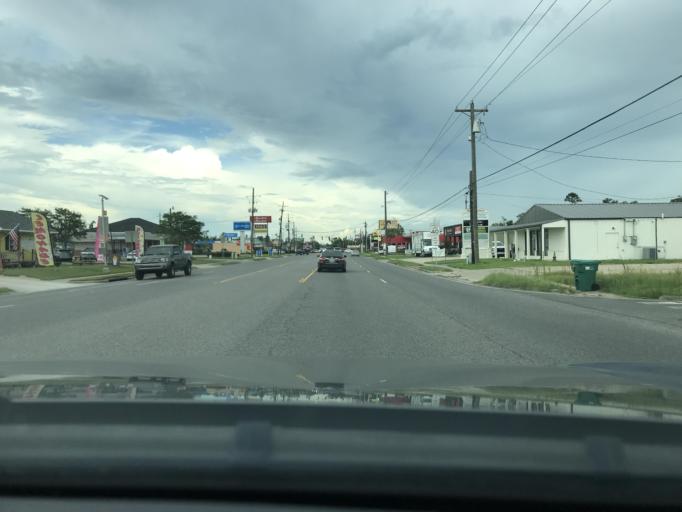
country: US
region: Louisiana
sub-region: Calcasieu Parish
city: Moss Bluff
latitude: 30.3006
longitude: -93.2024
